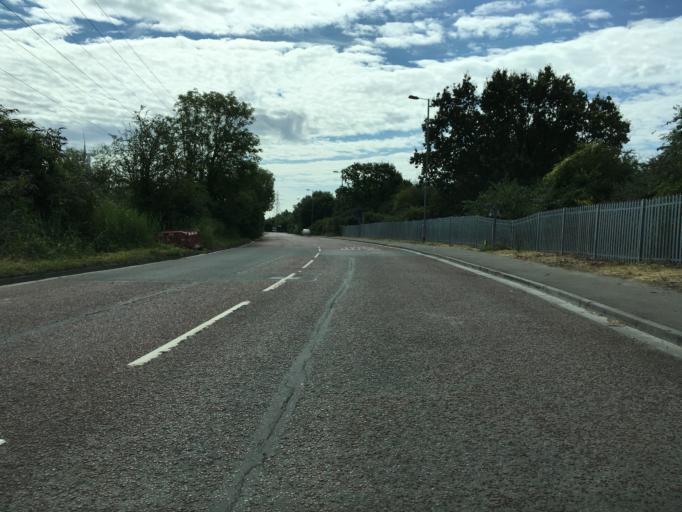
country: GB
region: Wales
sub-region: Newport
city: Nash
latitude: 51.5659
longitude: -2.9691
